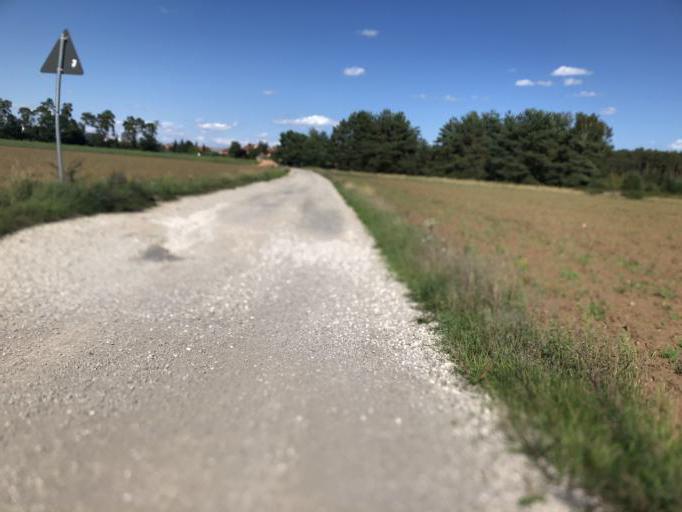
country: DE
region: Bavaria
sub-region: Regierungsbezirk Mittelfranken
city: Mohrendorf
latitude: 49.6280
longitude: 10.9884
